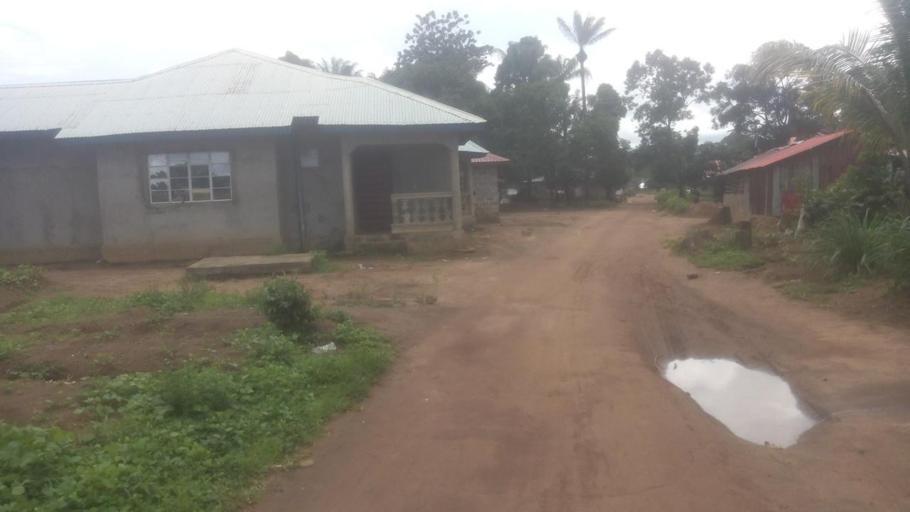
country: SL
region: Northern Province
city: Tintafor
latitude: 8.6372
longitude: -13.2192
